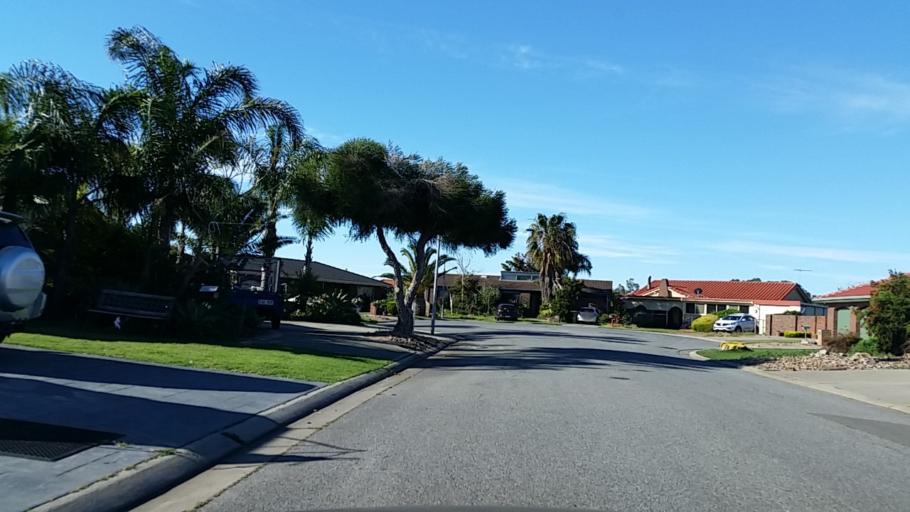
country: AU
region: South Australia
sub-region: Charles Sturt
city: West Lakes Shore
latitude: -34.8693
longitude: 138.4950
